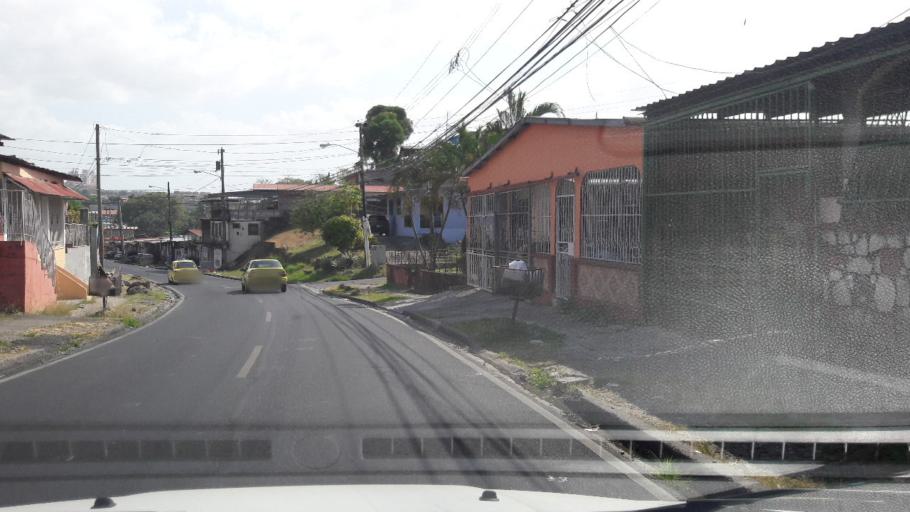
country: PA
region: Panama
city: San Miguelito
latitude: 9.0420
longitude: -79.4959
